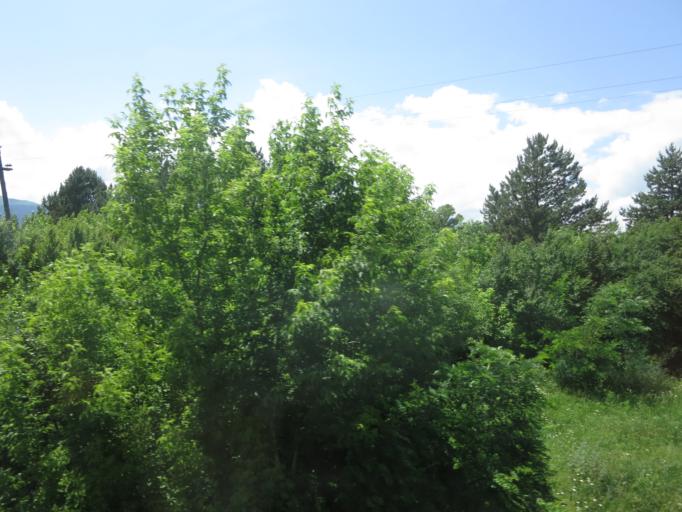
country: GE
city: Agara
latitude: 42.0155
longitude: 43.9144
